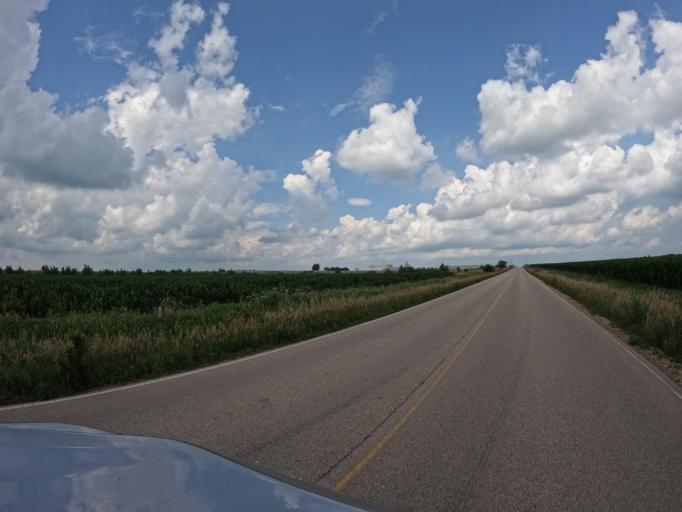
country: US
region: Iowa
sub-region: Clinton County
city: Camanche
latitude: 41.8011
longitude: -90.3351
